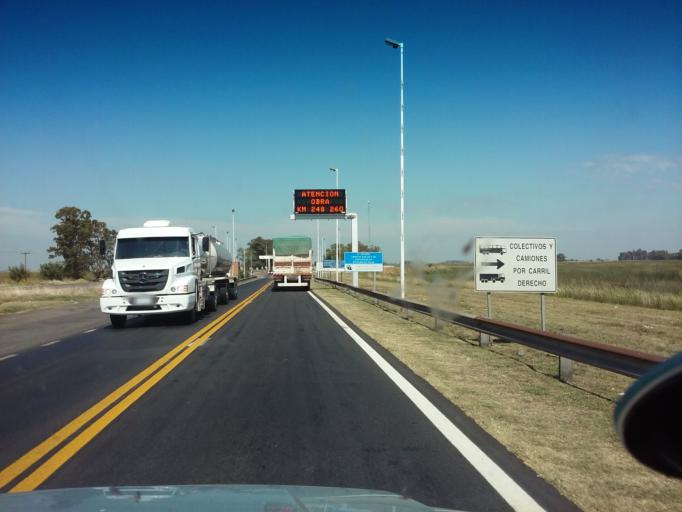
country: AR
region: Buenos Aires
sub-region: Partido de Nueve de Julio
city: Nueve de Julio
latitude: -35.3588
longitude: -60.7010
